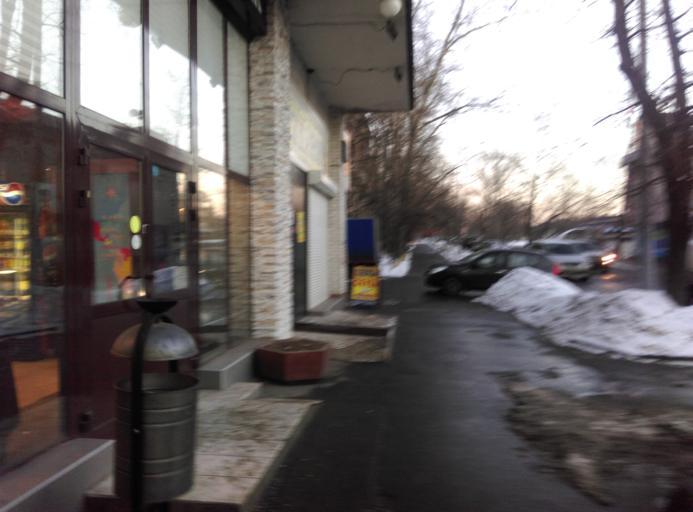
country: RU
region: Moskovskaya
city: Fili
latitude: 55.7348
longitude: 37.4886
